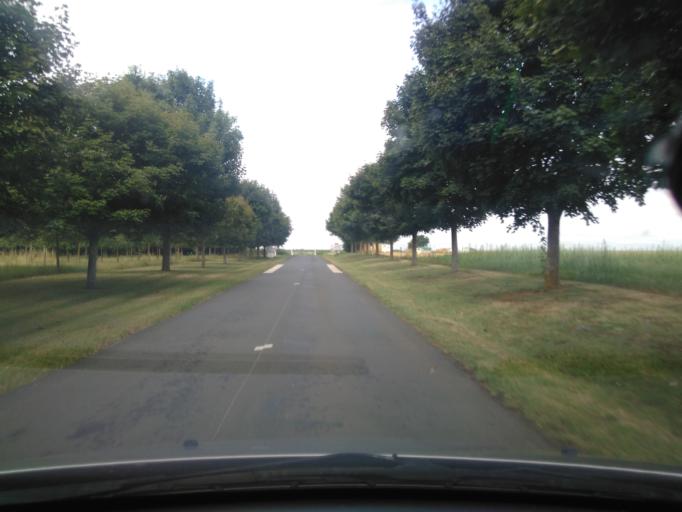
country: FR
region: Pays de la Loire
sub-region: Departement de la Vendee
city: Sainte-Hermine
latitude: 46.5101
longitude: -1.0650
